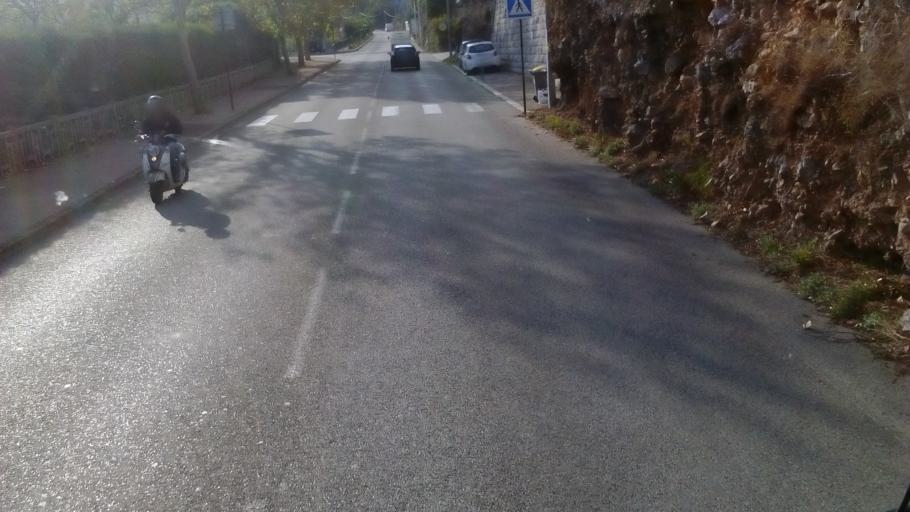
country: MC
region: Commune de Monaco
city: Saint-Roman
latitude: 43.7545
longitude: 7.4447
